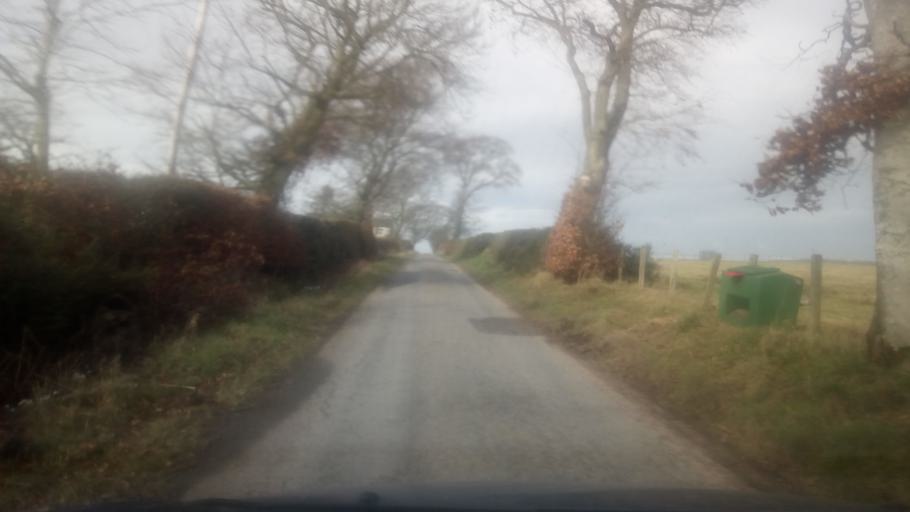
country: GB
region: Scotland
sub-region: The Scottish Borders
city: Jedburgh
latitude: 55.4119
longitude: -2.6494
